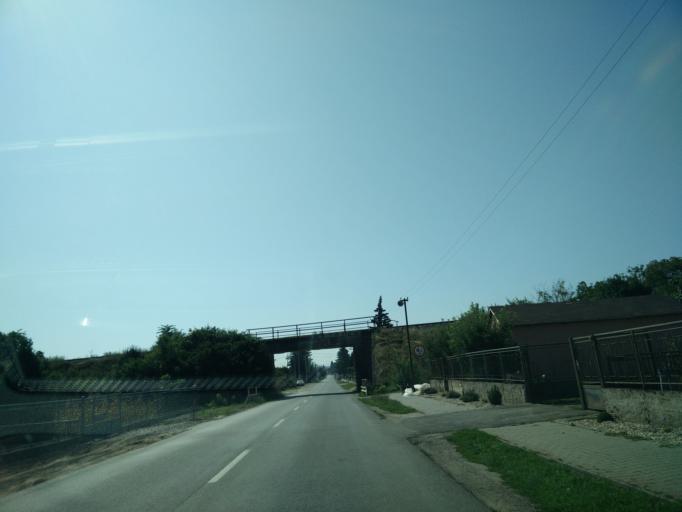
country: SK
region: Nitriansky
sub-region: Okres Nitra
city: Nitra
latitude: 48.3427
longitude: 18.0303
